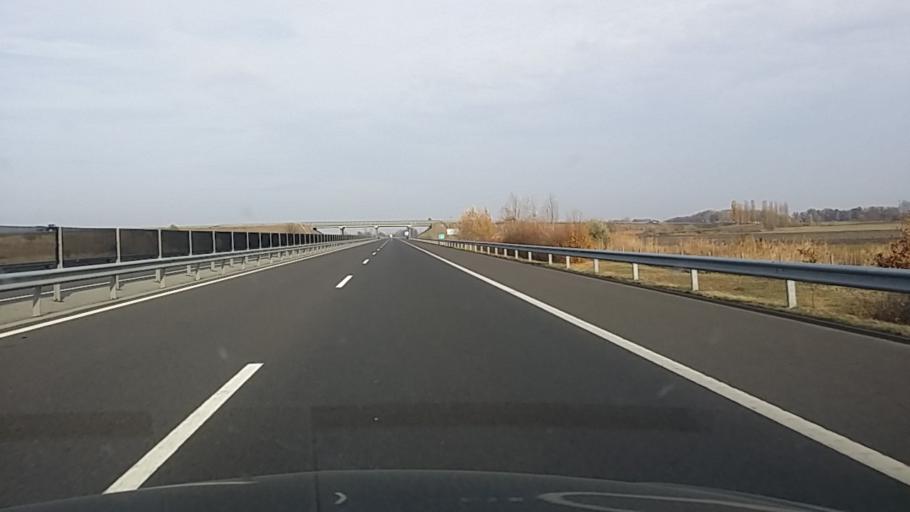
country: HU
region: Hajdu-Bihar
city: Gorbehaza
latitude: 47.8153
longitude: 21.3118
